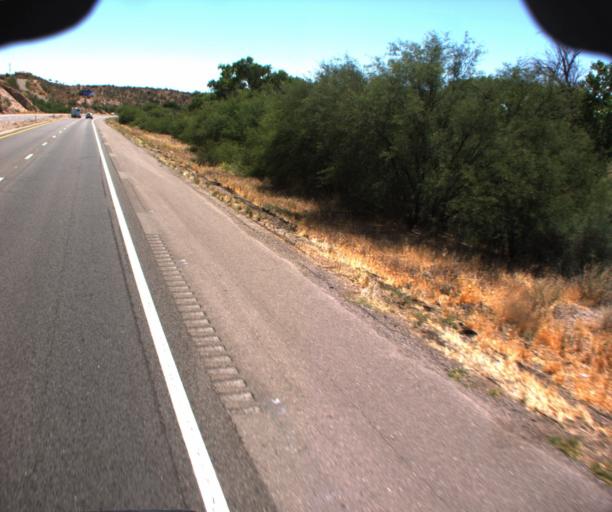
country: US
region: Arizona
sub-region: Maricopa County
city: Wickenburg
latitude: 33.9011
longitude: -112.6704
